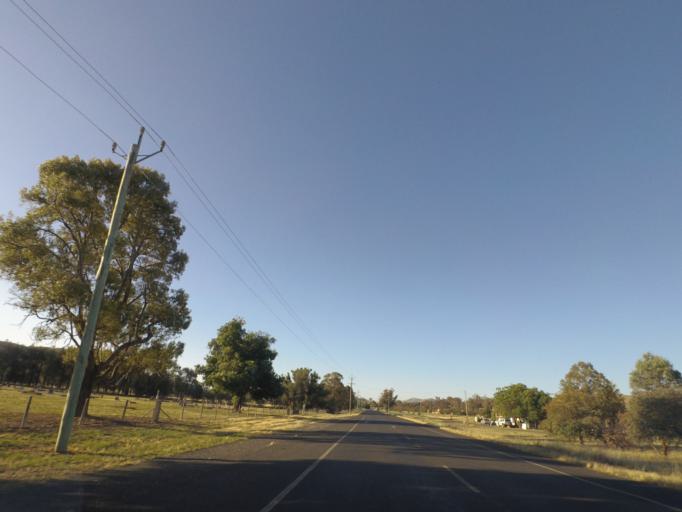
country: AU
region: New South Wales
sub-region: Gundagai
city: Gundagai
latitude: -34.9322
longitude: 148.1668
